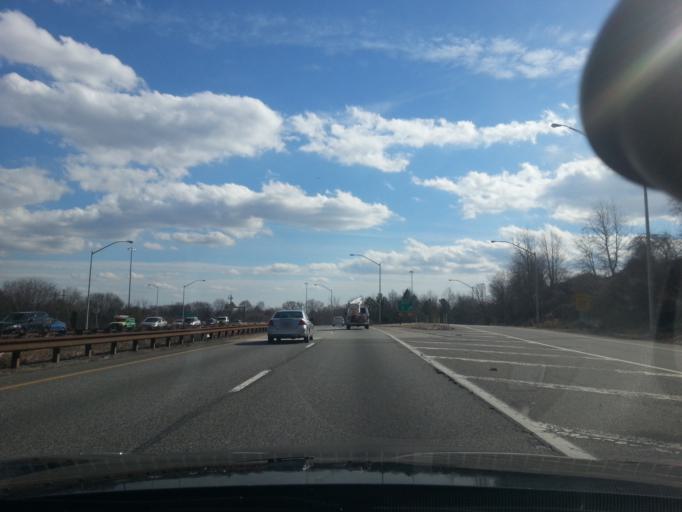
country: US
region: Pennsylvania
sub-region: Delaware County
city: Woodlyn
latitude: 39.8765
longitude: -75.3515
